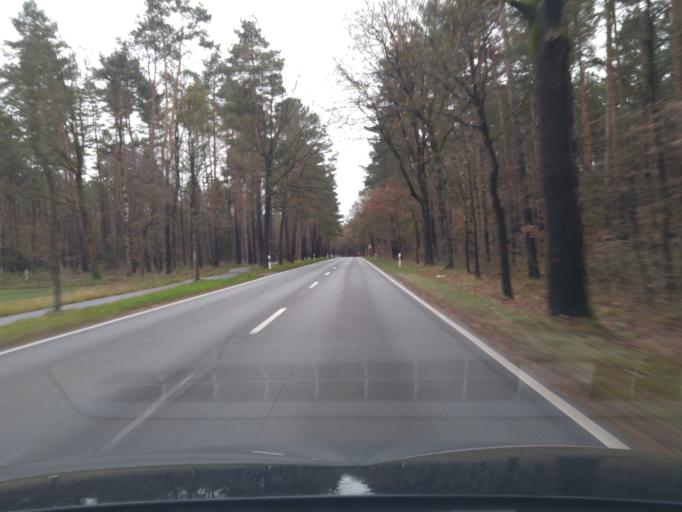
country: DE
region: Lower Saxony
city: Winsen
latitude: 52.7248
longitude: 9.9251
